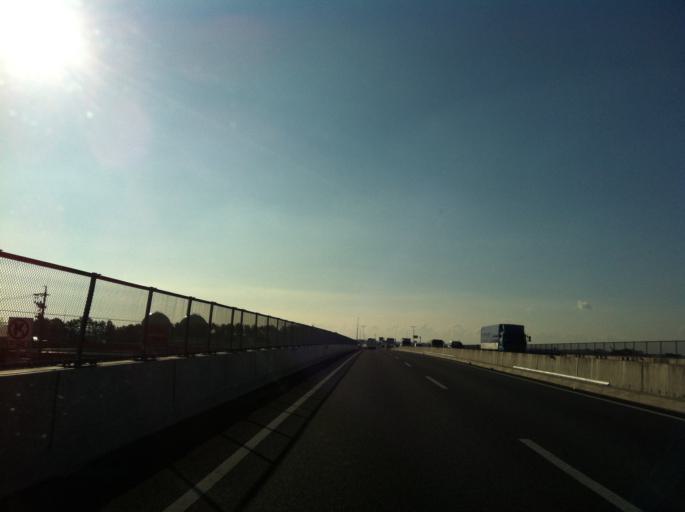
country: JP
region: Aichi
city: Kozakai-cho
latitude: 34.7621
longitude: 137.3326
